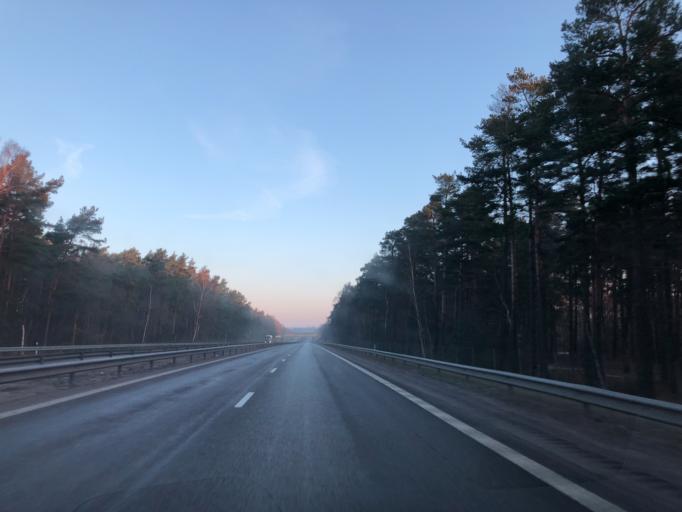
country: SE
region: Halland
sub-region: Halmstads Kommun
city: Fyllinge
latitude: 56.6811
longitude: 12.8954
